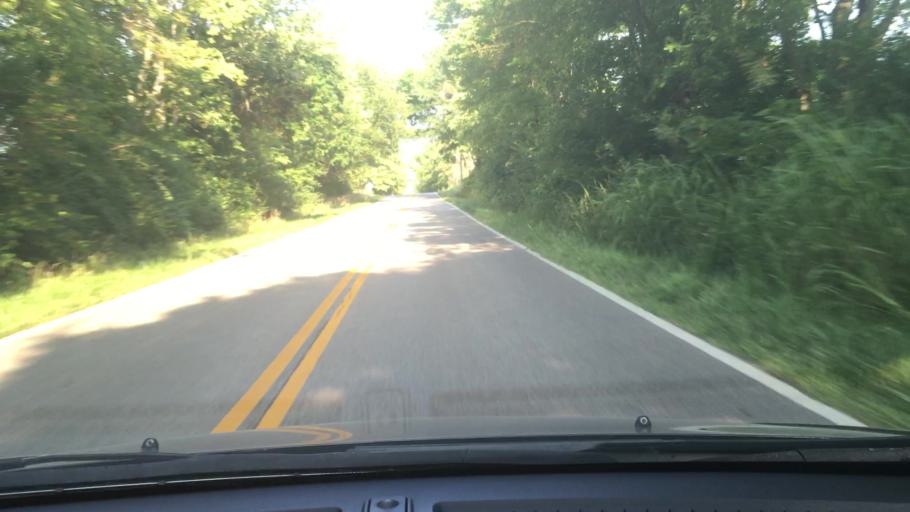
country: US
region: Missouri
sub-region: Jackson County
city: Lees Summit
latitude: 38.8907
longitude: -94.4315
